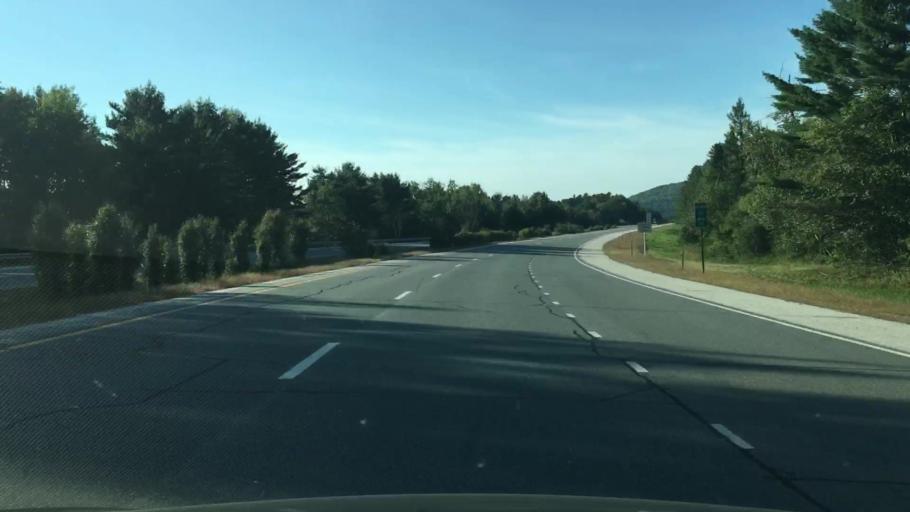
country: US
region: New Hampshire
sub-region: Grafton County
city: Littleton
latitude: 44.2307
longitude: -71.7515
